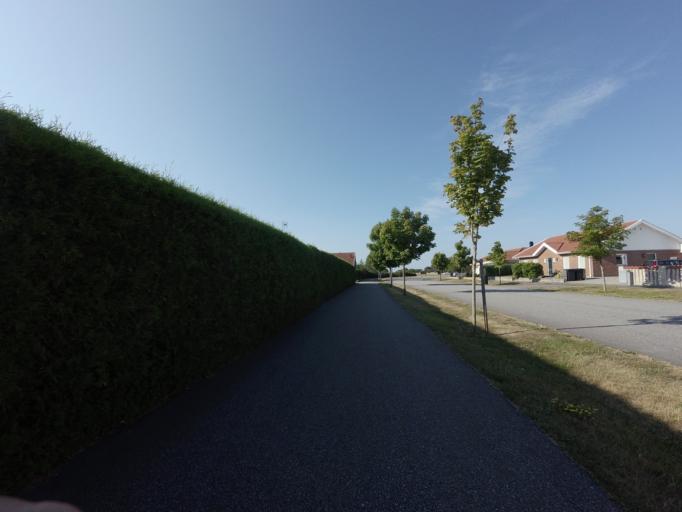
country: SE
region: Skane
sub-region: Trelleborgs Kommun
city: Trelleborg
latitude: 55.3625
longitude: 13.2271
